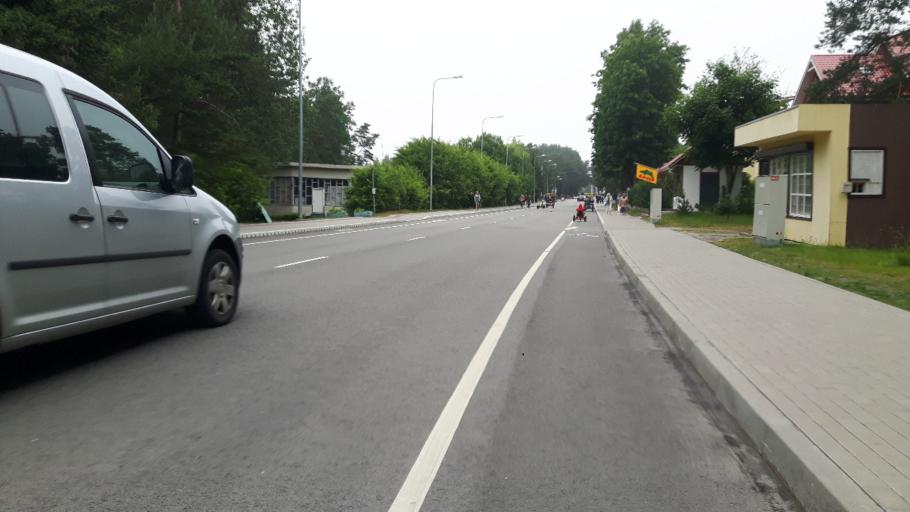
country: LT
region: Klaipedos apskritis
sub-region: Palanga
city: Sventoji
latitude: 56.0250
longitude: 21.0792
